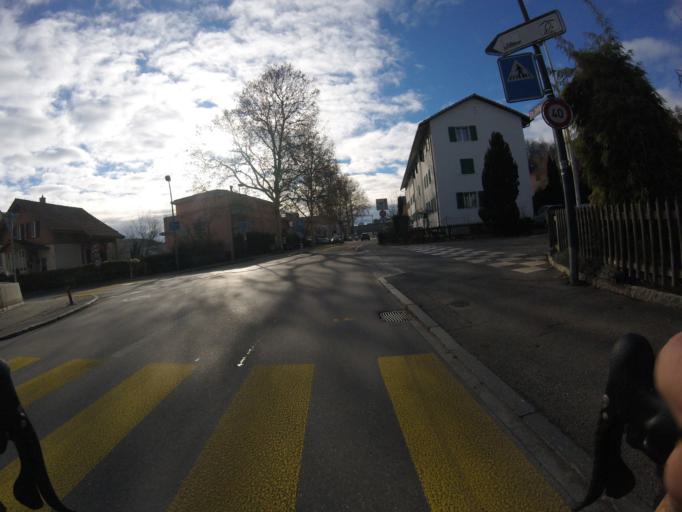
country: CH
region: Bern
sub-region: Bern-Mittelland District
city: Muri
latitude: 46.9514
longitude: 7.4852
